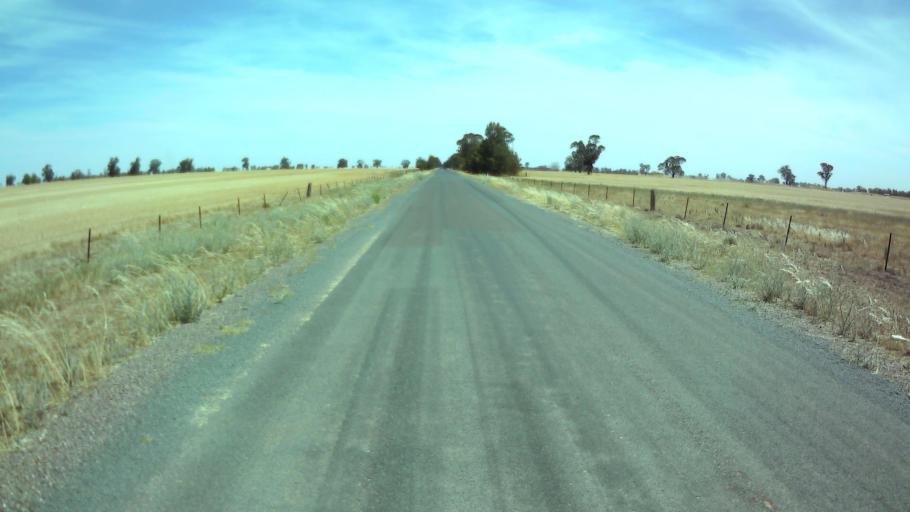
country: AU
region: New South Wales
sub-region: Weddin
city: Grenfell
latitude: -33.9121
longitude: 147.7657
